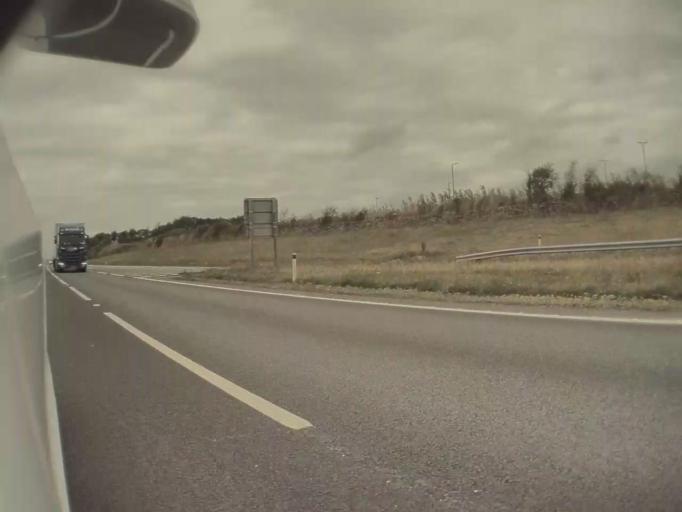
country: GB
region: Wales
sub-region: Anglesey
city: Llanfachraeth
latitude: 53.2764
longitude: -4.5174
